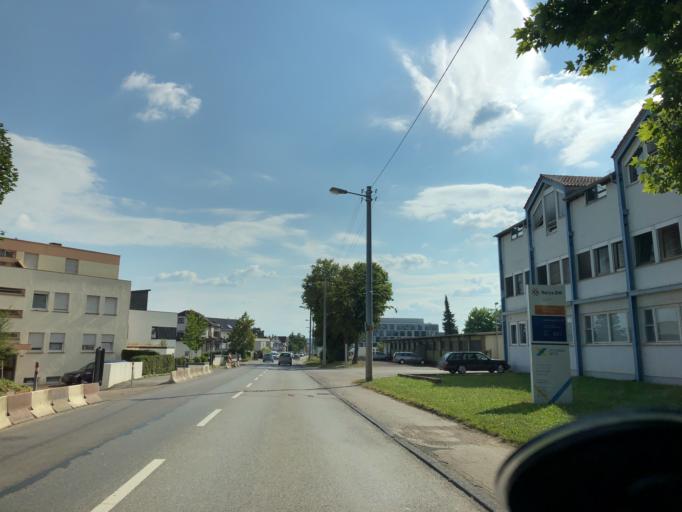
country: DE
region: Baden-Wuerttemberg
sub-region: Regierungsbezirk Stuttgart
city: Leinfelden-Echterdingen
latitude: 48.7329
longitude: 9.1588
